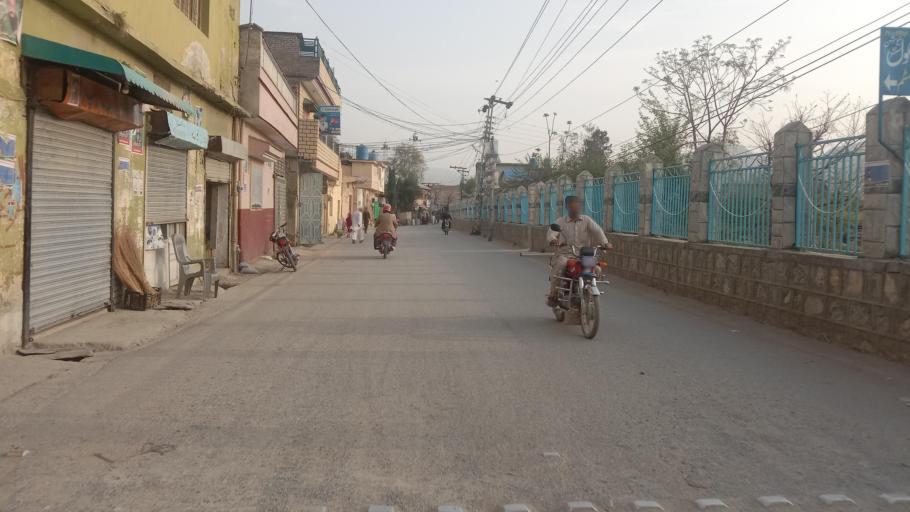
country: PK
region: Khyber Pakhtunkhwa
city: Abbottabad
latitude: 34.1669
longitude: 73.2596
